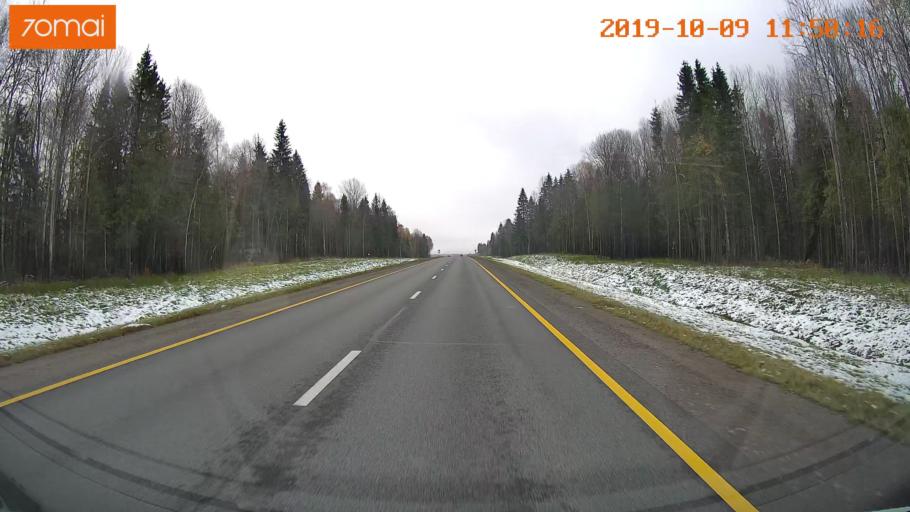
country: RU
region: Vologda
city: Gryazovets
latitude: 58.8076
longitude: 40.2438
